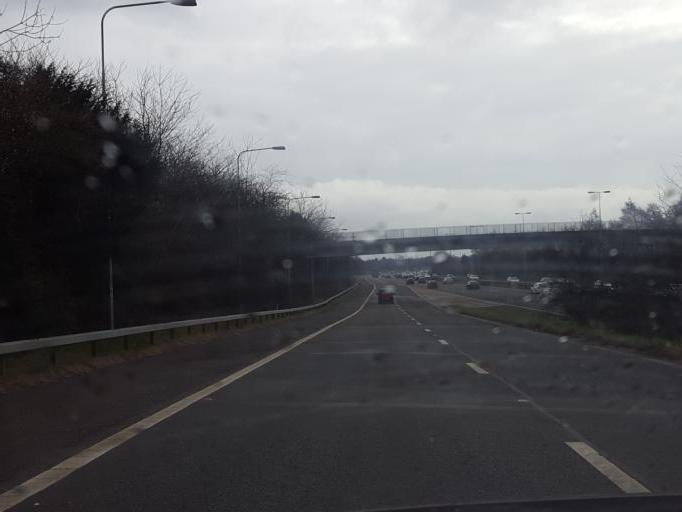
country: GB
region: England
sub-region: Buckinghamshire
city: Stokenchurch
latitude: 51.6601
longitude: -0.9098
